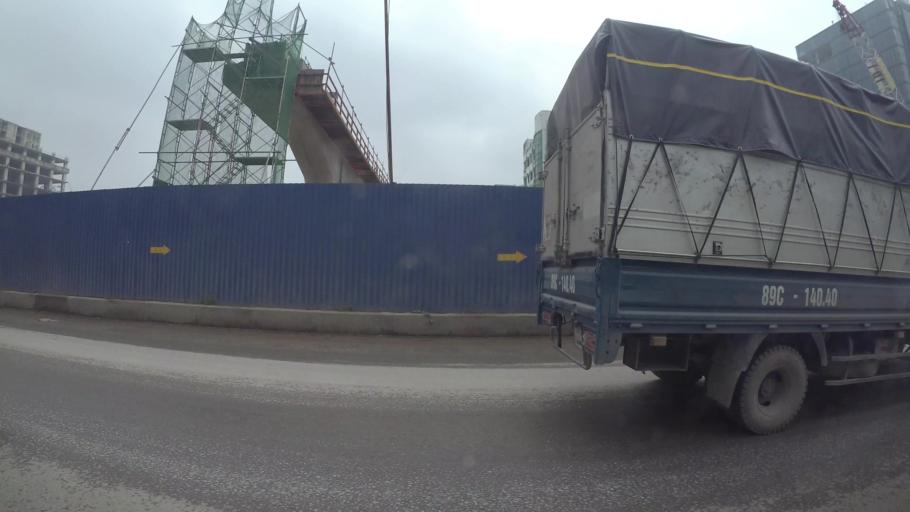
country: VN
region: Ha Noi
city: Cau Dien
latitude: 21.0513
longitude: 105.7815
